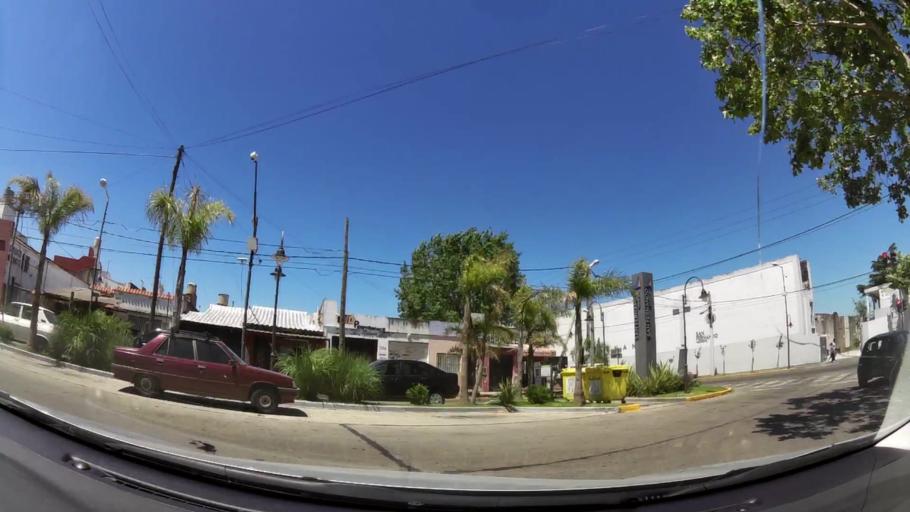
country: AR
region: Buenos Aires
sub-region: Partido de Tigre
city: Tigre
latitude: -34.4564
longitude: -58.5512
